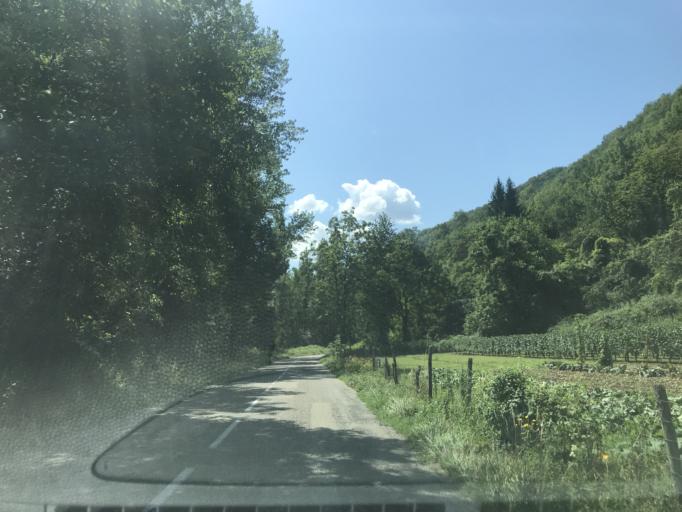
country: FR
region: Rhone-Alpes
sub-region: Departement de la Savoie
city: Chatillon
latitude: 45.8131
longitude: 5.8145
